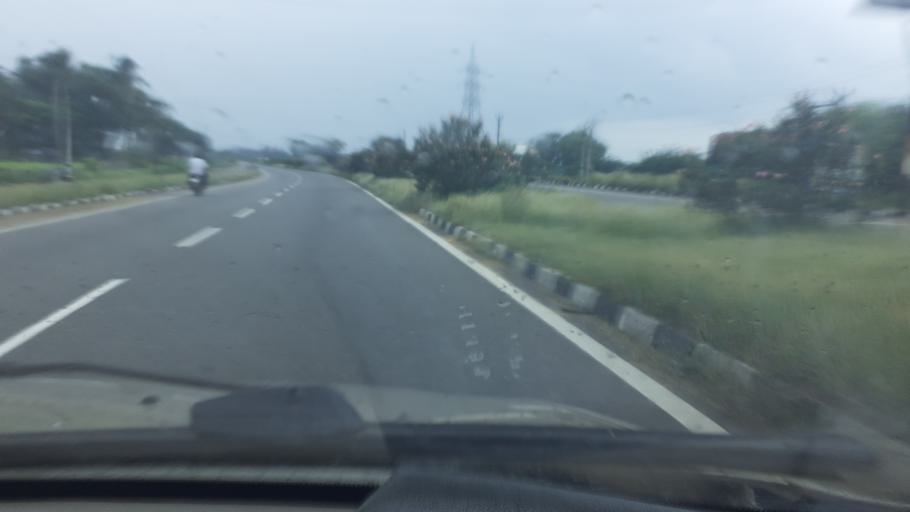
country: IN
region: Tamil Nadu
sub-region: Virudhunagar
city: Virudunagar
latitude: 9.6374
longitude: 77.9614
